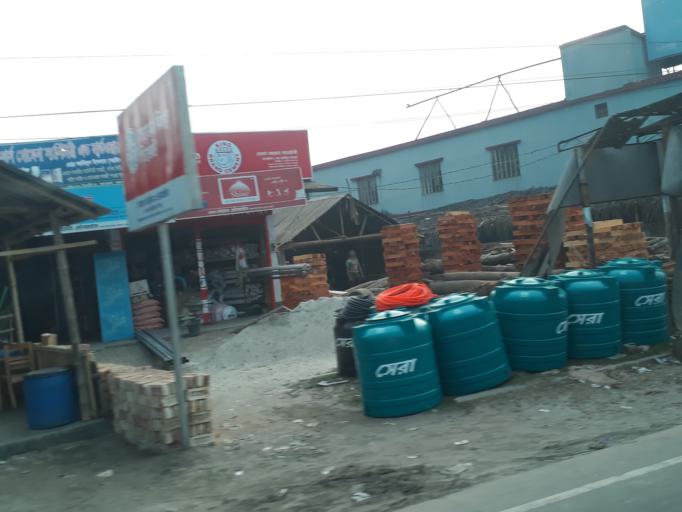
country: BD
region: Khulna
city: Bhatpara Abhaynagar
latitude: 22.9825
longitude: 89.4502
